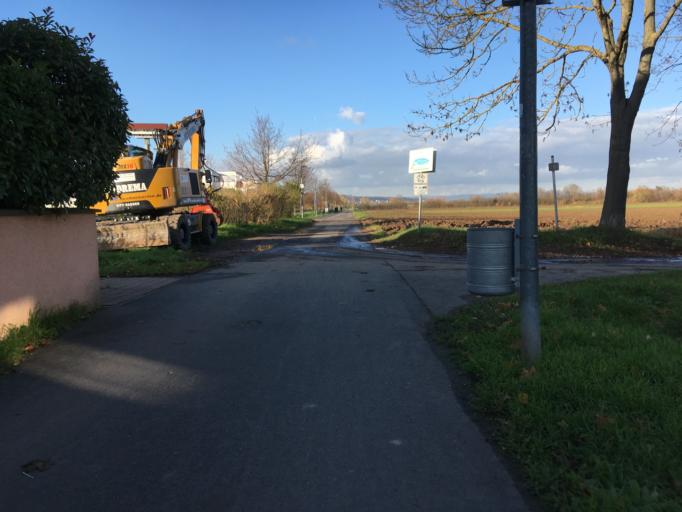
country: DE
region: Rheinland-Pfalz
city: Nackenheim
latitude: 49.9232
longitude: 8.3370
